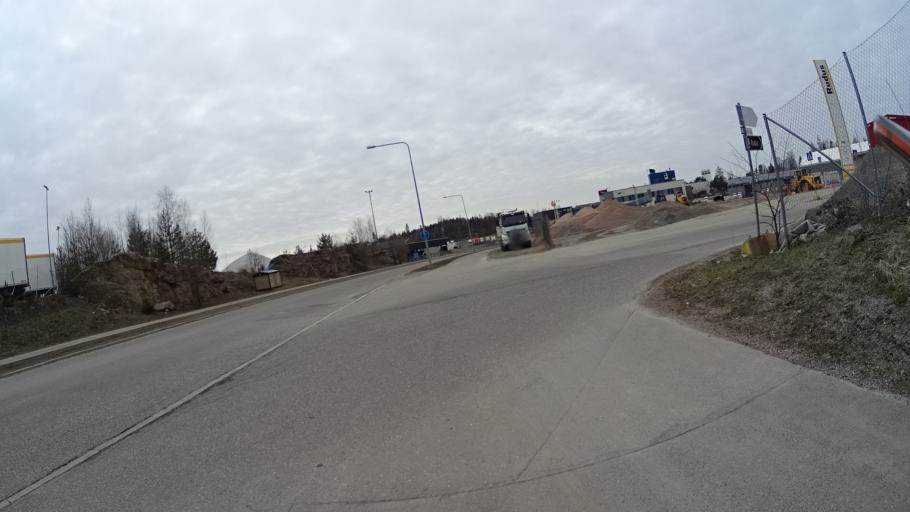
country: FI
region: Uusimaa
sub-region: Helsinki
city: Teekkarikylae
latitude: 60.3022
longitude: 24.9066
